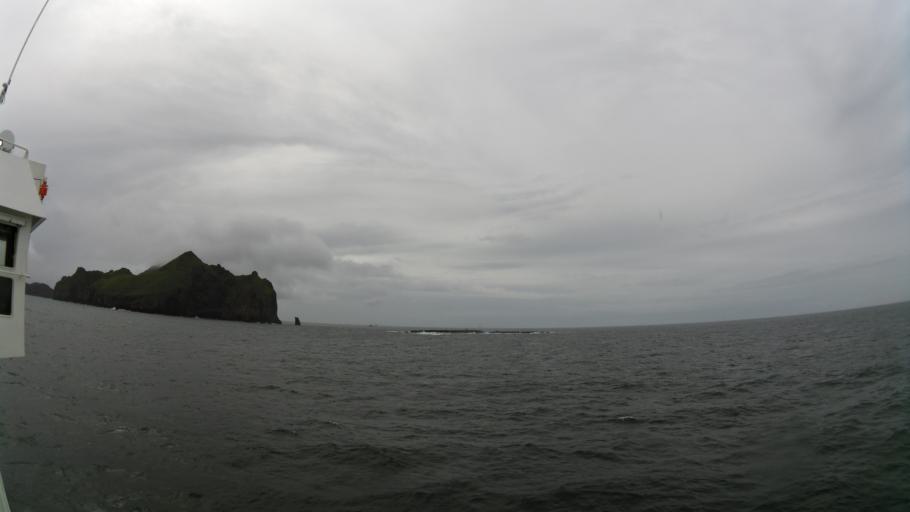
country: IS
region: South
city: Vestmannaeyjar
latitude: 63.4593
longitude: -20.2207
